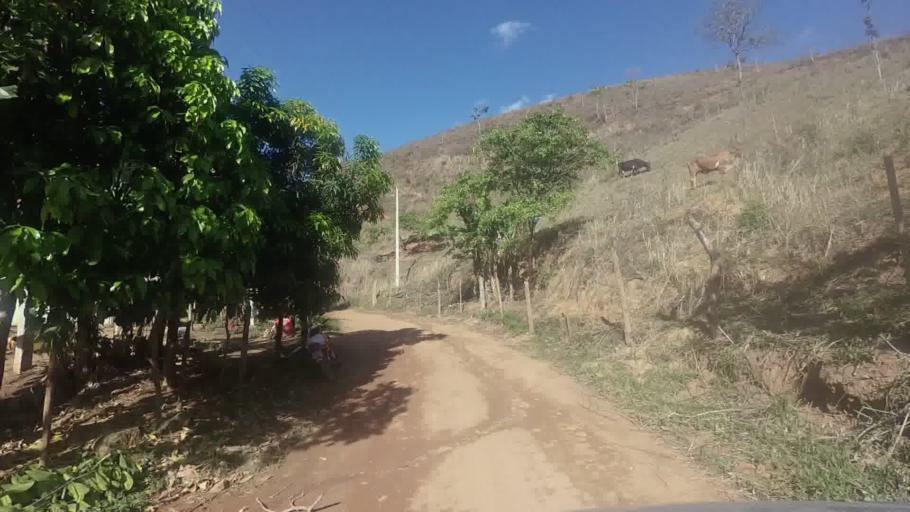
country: BR
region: Espirito Santo
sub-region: Sao Jose Do Calcado
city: Sao Jose do Calcado
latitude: -21.0327
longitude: -41.5941
